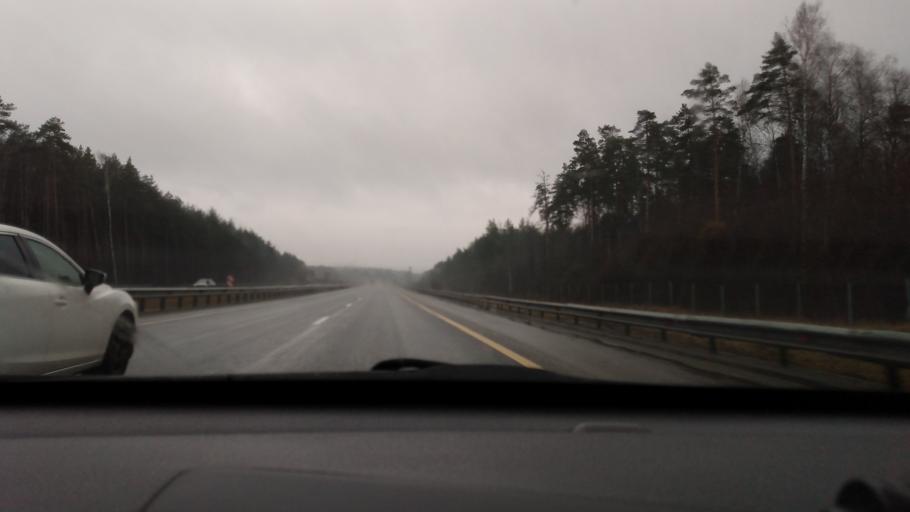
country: RU
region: Moskovskaya
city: Stupino
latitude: 54.8605
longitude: 38.0340
